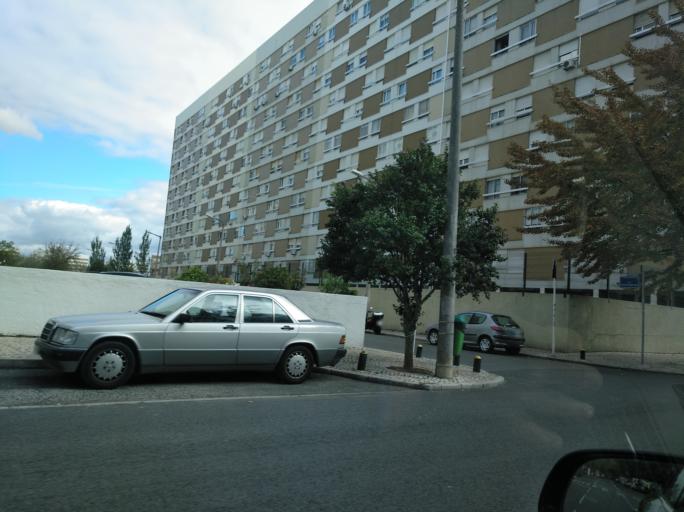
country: PT
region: Lisbon
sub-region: Loures
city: Sacavem
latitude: 38.7822
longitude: -9.1140
